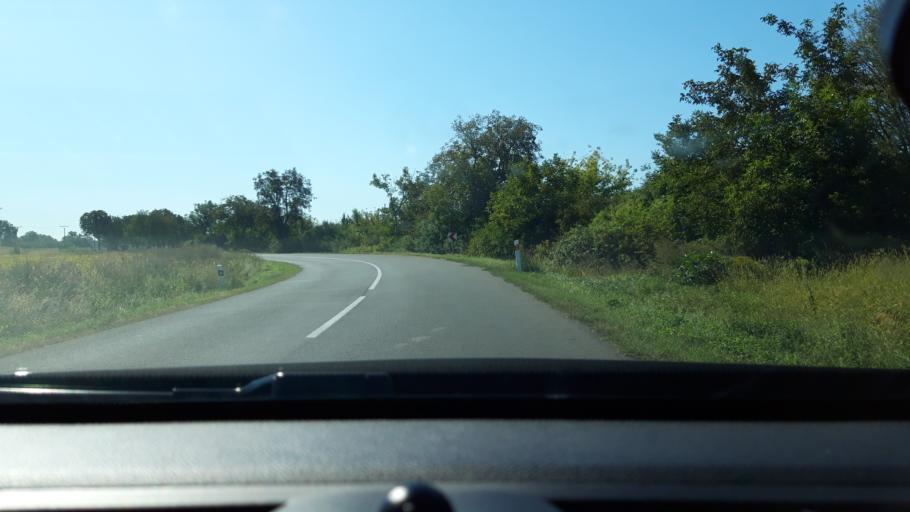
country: SK
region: Kosicky
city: Michalovce
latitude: 48.7261
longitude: 21.9183
